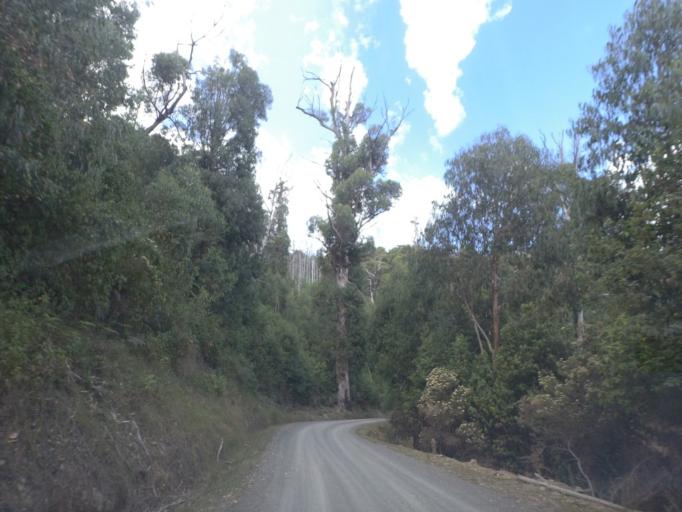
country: AU
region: Victoria
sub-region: Murrindindi
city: Alexandra
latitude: -37.4191
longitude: 145.7597
